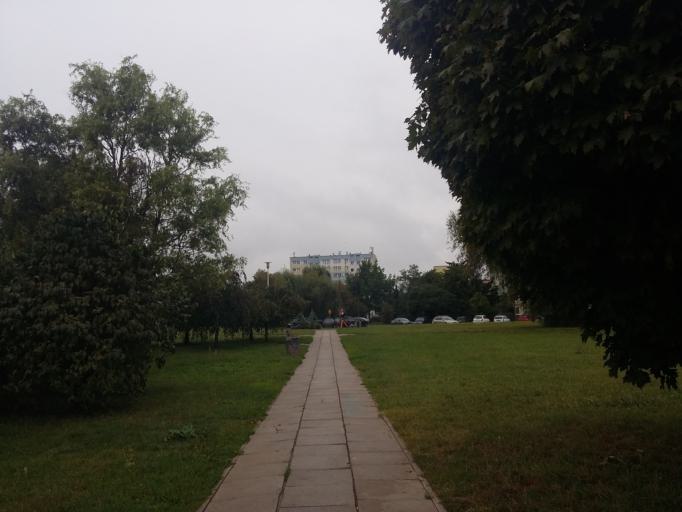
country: PL
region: Lodz Voivodeship
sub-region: Powiat pabianicki
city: Konstantynow Lodzki
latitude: 51.7467
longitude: 19.3886
